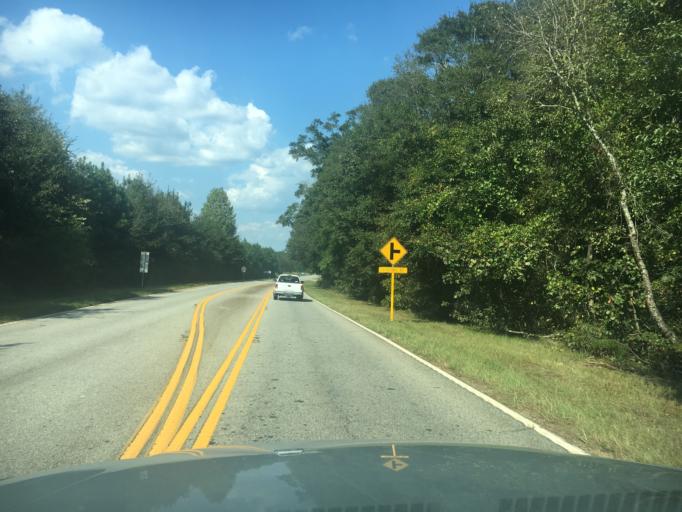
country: US
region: South Carolina
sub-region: Anderson County
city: Pendleton
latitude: 34.6153
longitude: -82.7838
